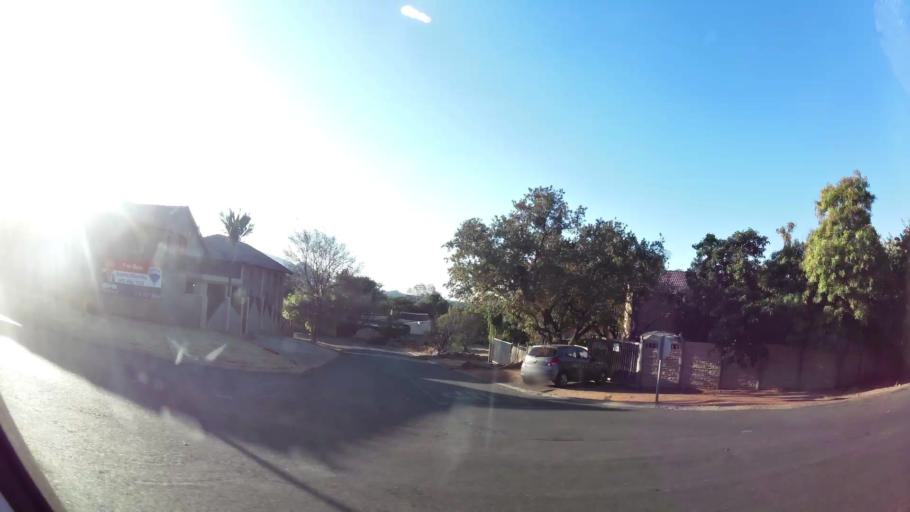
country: ZA
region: North-West
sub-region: Bojanala Platinum District Municipality
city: Rustenburg
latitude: -25.6891
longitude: 27.2089
